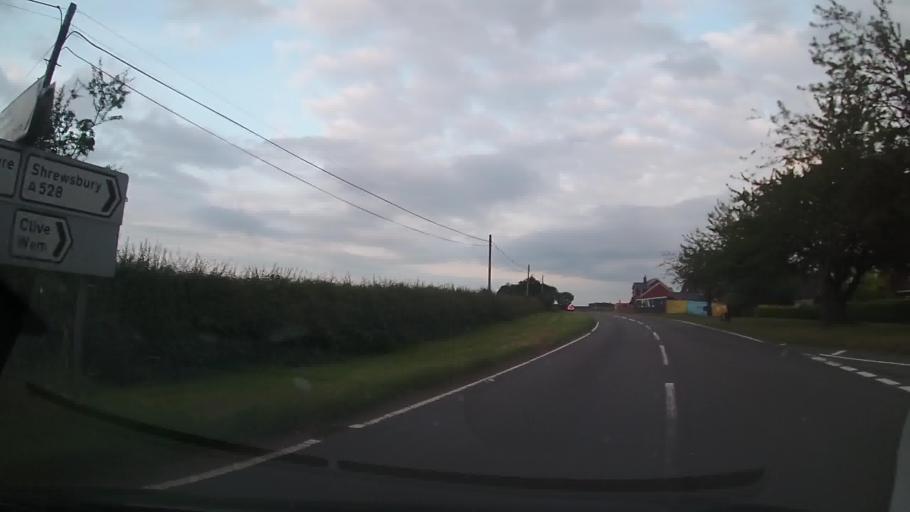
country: GB
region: England
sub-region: Shropshire
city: Petton
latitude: 52.8103
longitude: -2.7847
